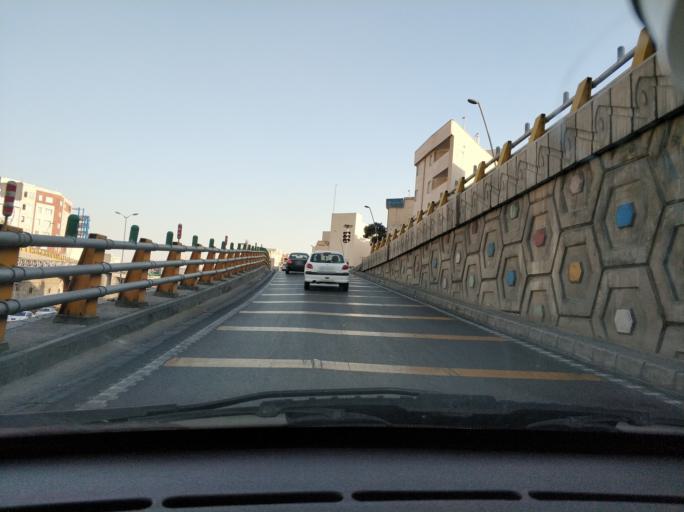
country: IR
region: Tehran
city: Tehran
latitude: 35.6889
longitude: 51.4570
